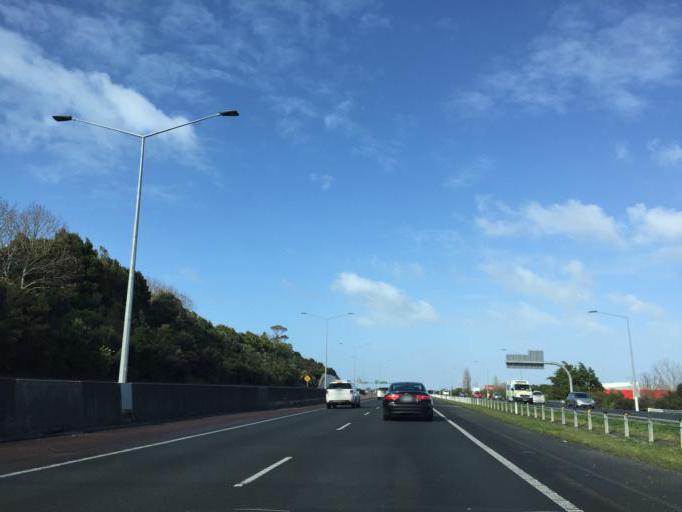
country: NZ
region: Auckland
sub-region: Auckland
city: North Shore
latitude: -36.7654
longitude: 174.7398
